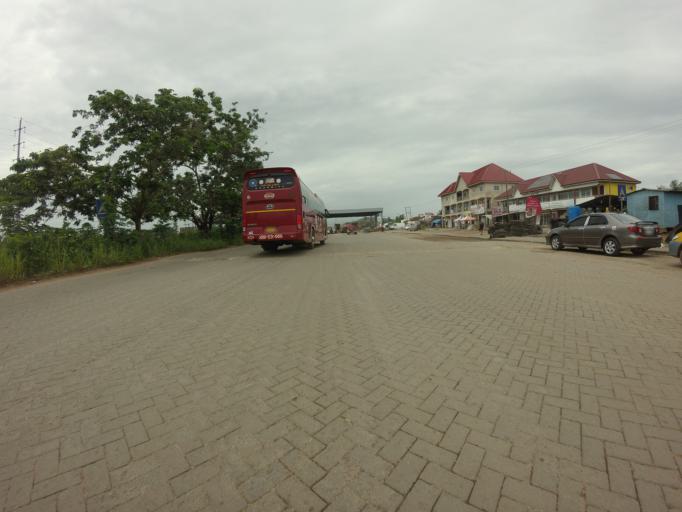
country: GH
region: Greater Accra
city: Achiaman
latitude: 5.7334
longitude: -0.3134
